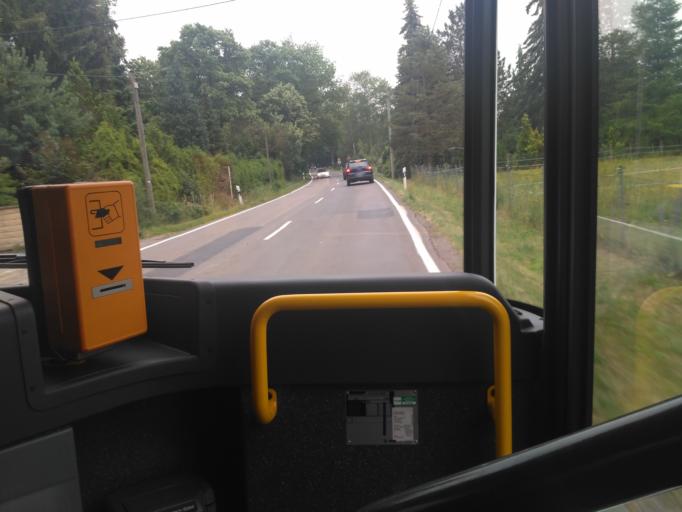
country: DE
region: Saxony
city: Weinbohla
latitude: 51.1627
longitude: 13.5998
